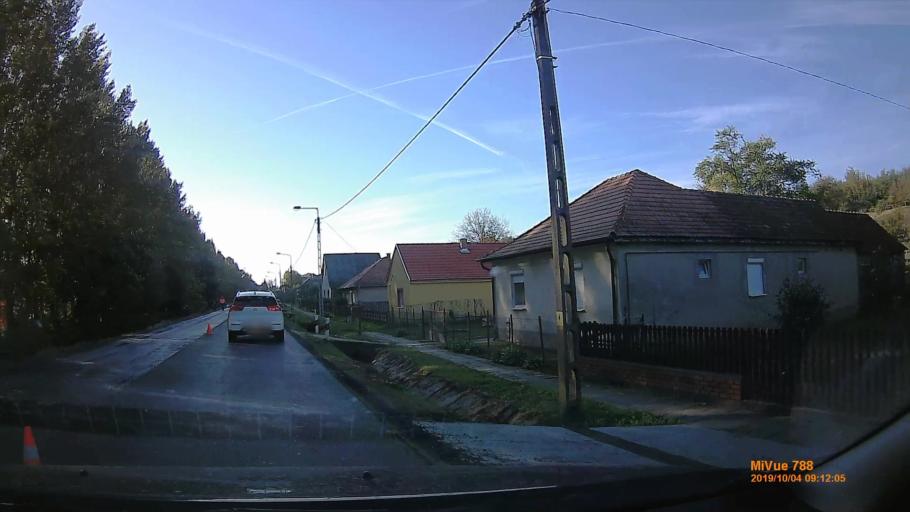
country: HU
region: Somogy
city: Karad
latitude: 46.6579
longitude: 17.7826
